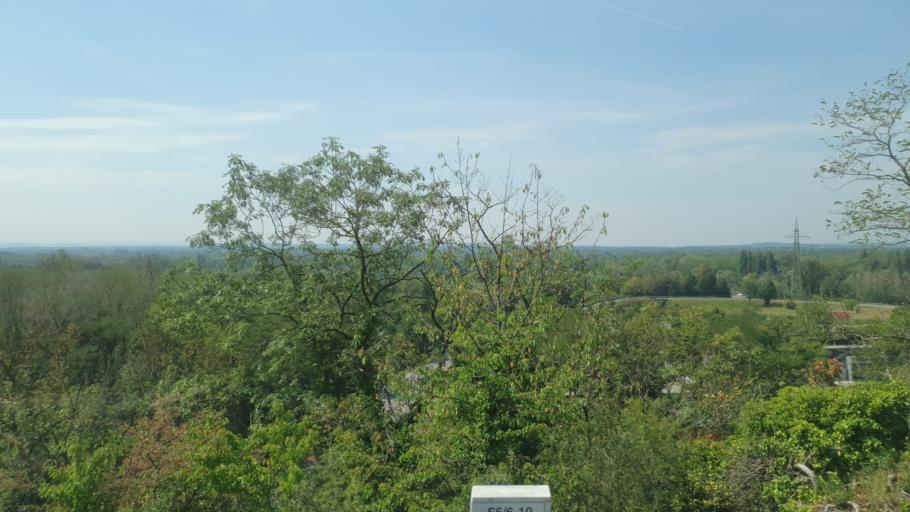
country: FR
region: Alsace
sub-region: Departement du Haut-Rhin
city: Kembs
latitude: 47.6786
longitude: 7.5276
